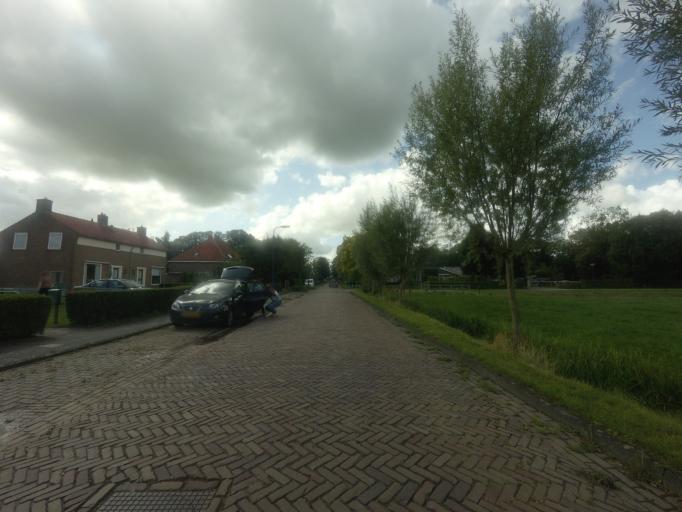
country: NL
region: Friesland
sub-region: Gemeente Littenseradiel
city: Makkum
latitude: 53.0893
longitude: 5.6993
